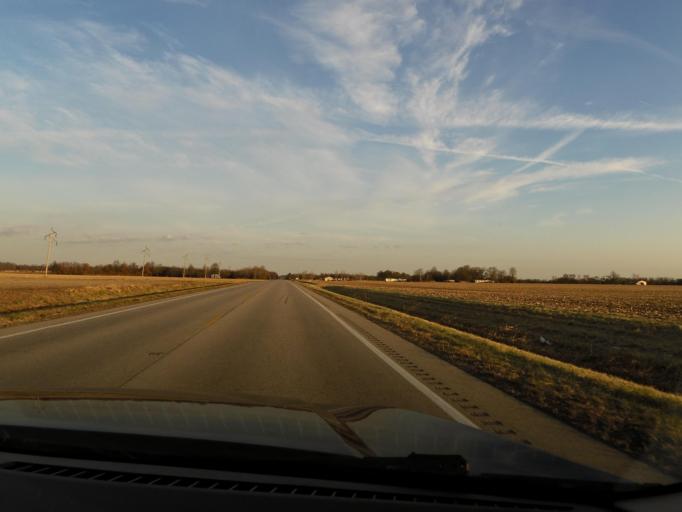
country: US
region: Illinois
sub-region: Fayette County
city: Vandalia
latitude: 38.8407
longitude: -89.0879
